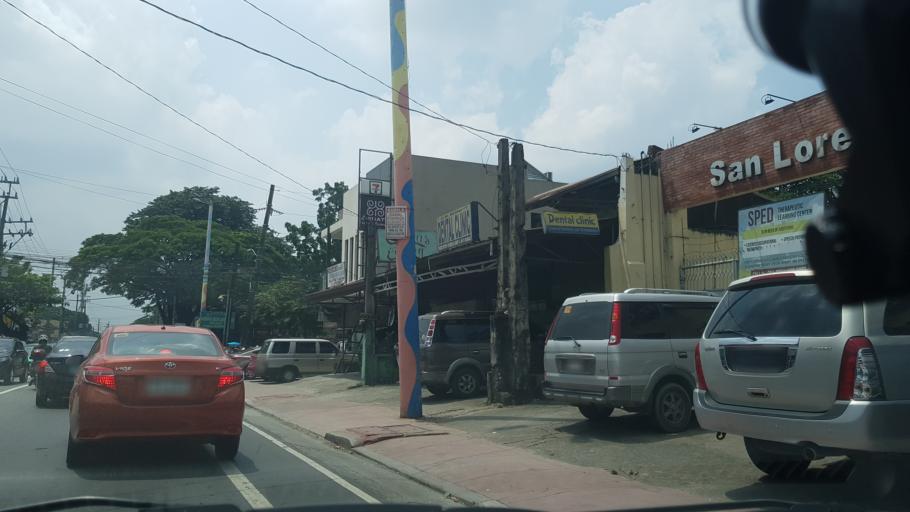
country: PH
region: Calabarzon
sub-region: Province of Rizal
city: San Mateo
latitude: 14.6703
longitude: 121.1085
